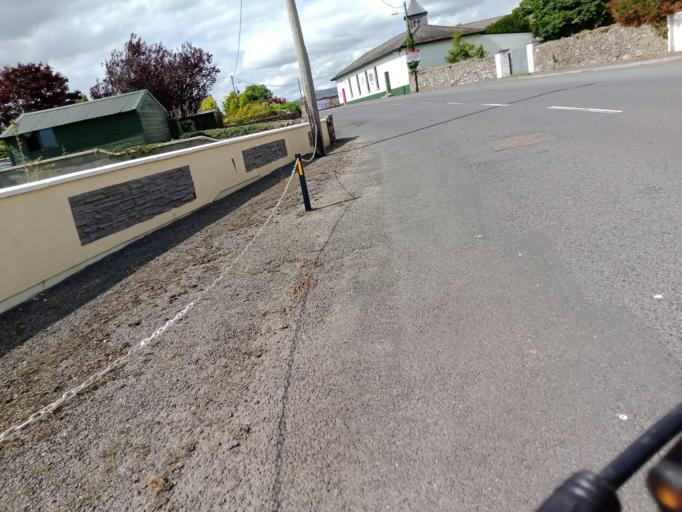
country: IE
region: Munster
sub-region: Waterford
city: Dungarvan
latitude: 52.1353
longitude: -7.4666
